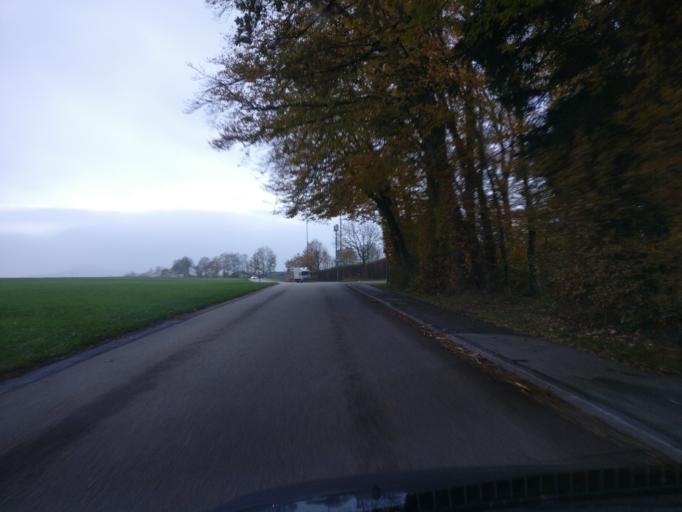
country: AT
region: Salzburg
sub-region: Politischer Bezirk Salzburg-Umgebung
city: Hallwang
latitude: 47.8494
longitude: 13.0920
